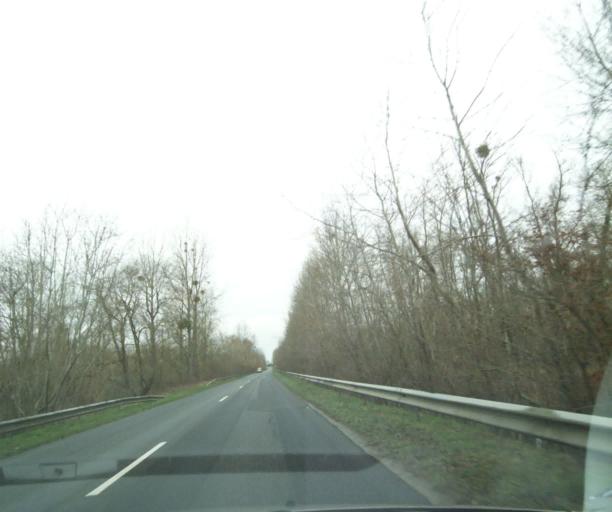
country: FR
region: Picardie
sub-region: Departement de l'Oise
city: Noyon
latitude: 49.5615
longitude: 3.0339
